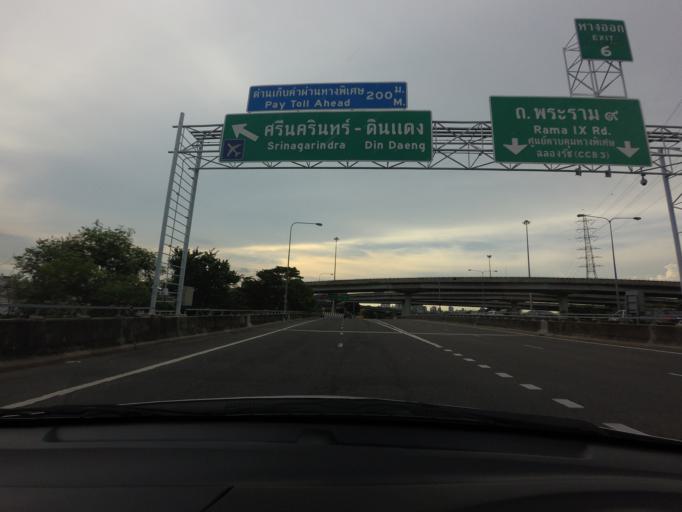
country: TH
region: Bangkok
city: Watthana
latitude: 13.7528
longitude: 100.5986
